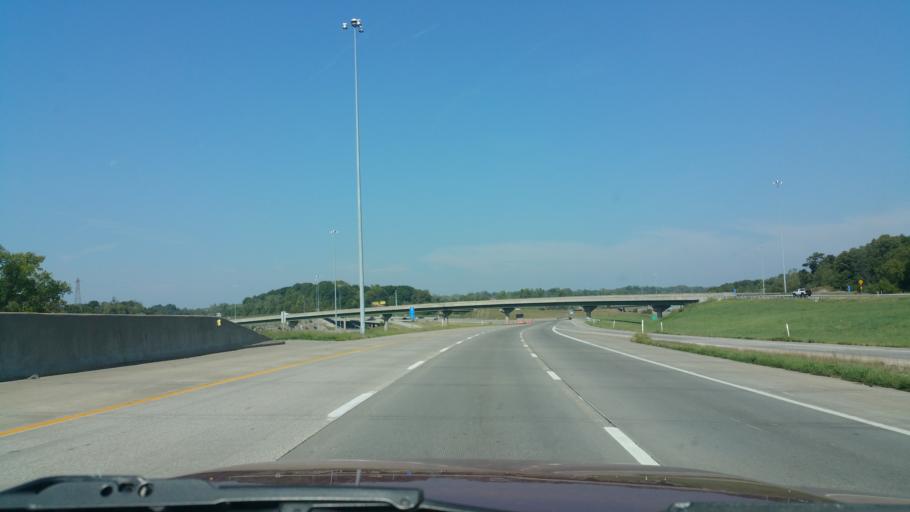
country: US
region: Kansas
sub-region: Wyandotte County
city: Kansas City
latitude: 39.1028
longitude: -94.6740
